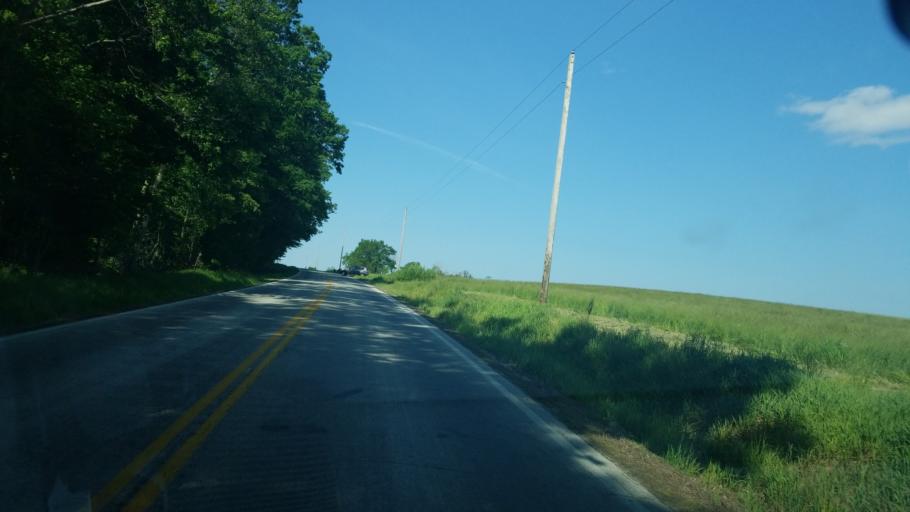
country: US
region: Ohio
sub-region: Ashland County
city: Loudonville
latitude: 40.7166
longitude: -82.2253
